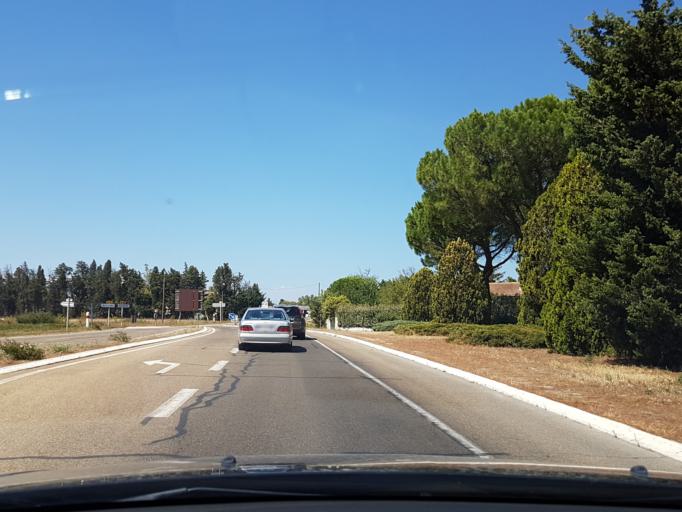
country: FR
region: Provence-Alpes-Cote d'Azur
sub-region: Departement des Bouches-du-Rhone
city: Eyragues
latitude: 43.8616
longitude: 4.8402
